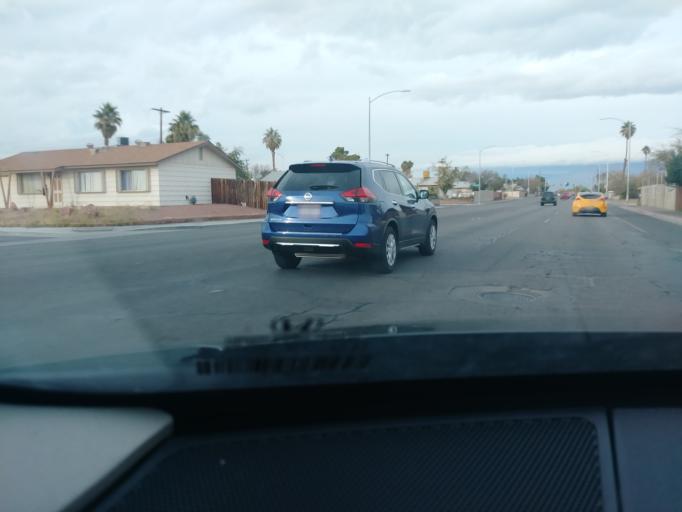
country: US
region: Nevada
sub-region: Clark County
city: Spring Valley
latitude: 36.1778
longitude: -115.2239
